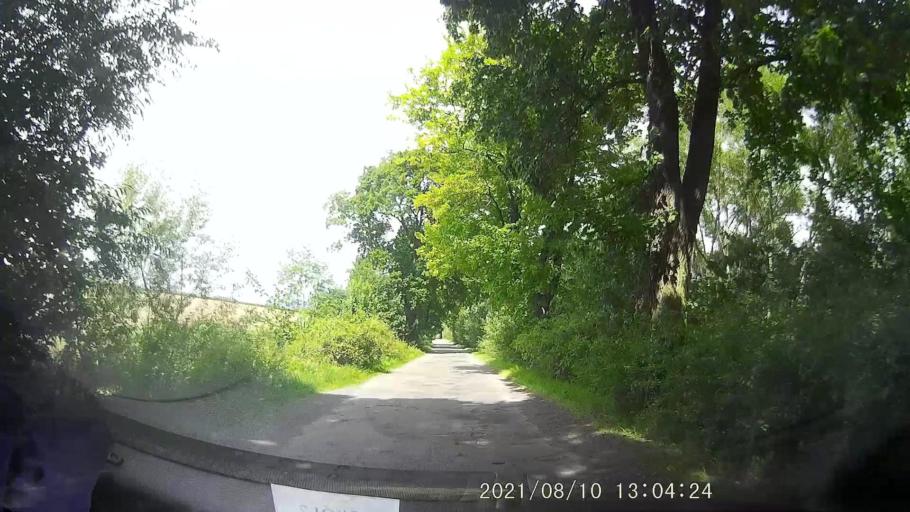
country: PL
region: Lower Silesian Voivodeship
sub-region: Powiat klodzki
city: Bozkow
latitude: 50.4764
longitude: 16.5644
